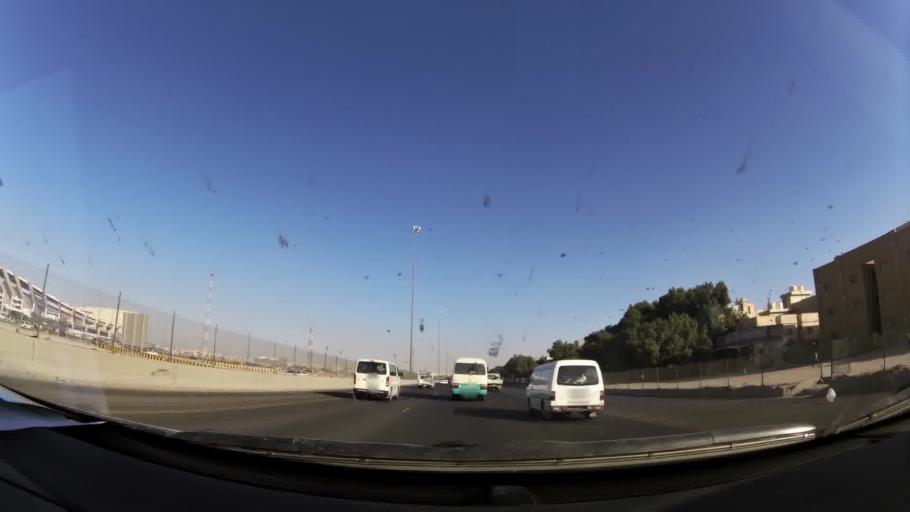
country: KW
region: Al Asimah
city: Ar Rabiyah
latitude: 29.2671
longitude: 47.9152
